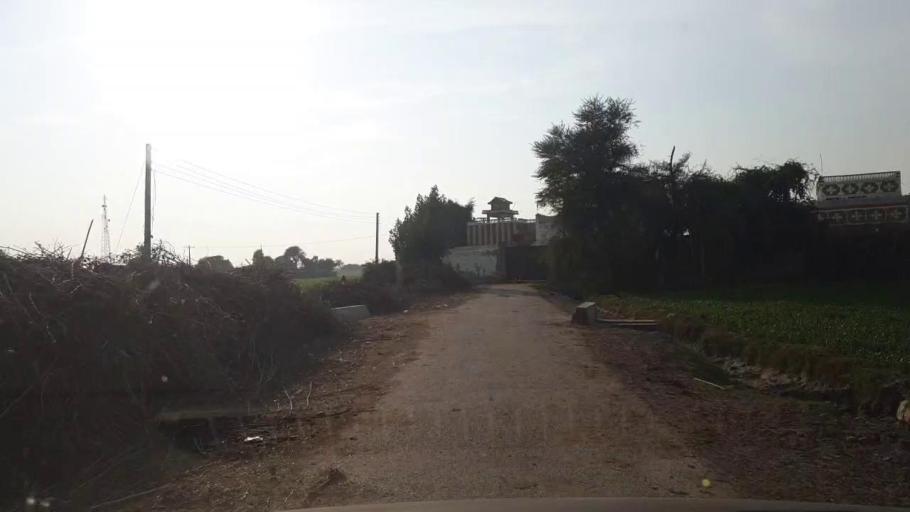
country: PK
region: Sindh
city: Shahpur Chakar
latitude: 26.1652
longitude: 68.6372
